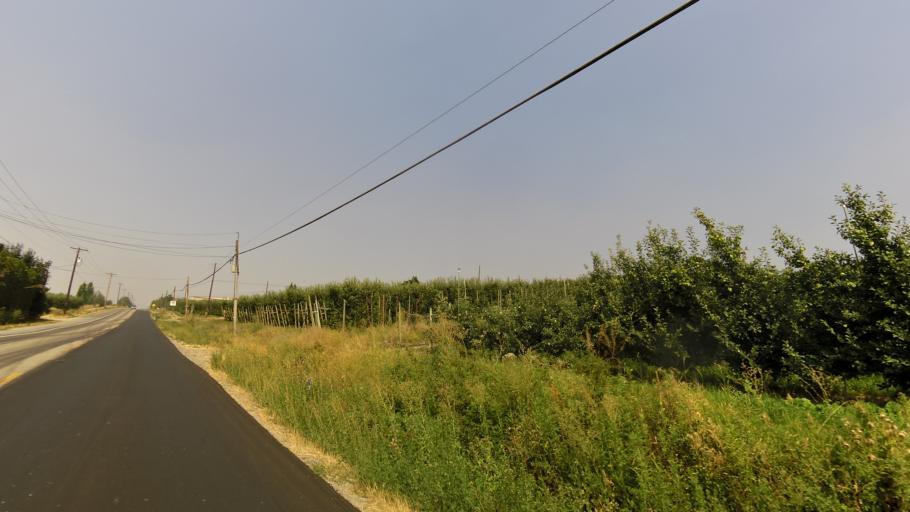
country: CA
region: British Columbia
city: Kelowna
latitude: 49.9273
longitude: -119.3641
